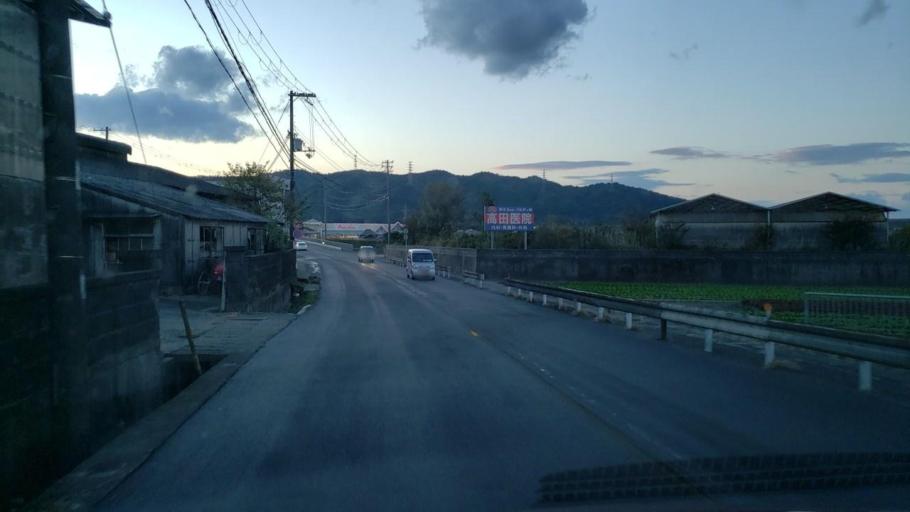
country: JP
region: Hyogo
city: Fukura
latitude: 34.3022
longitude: 134.7498
